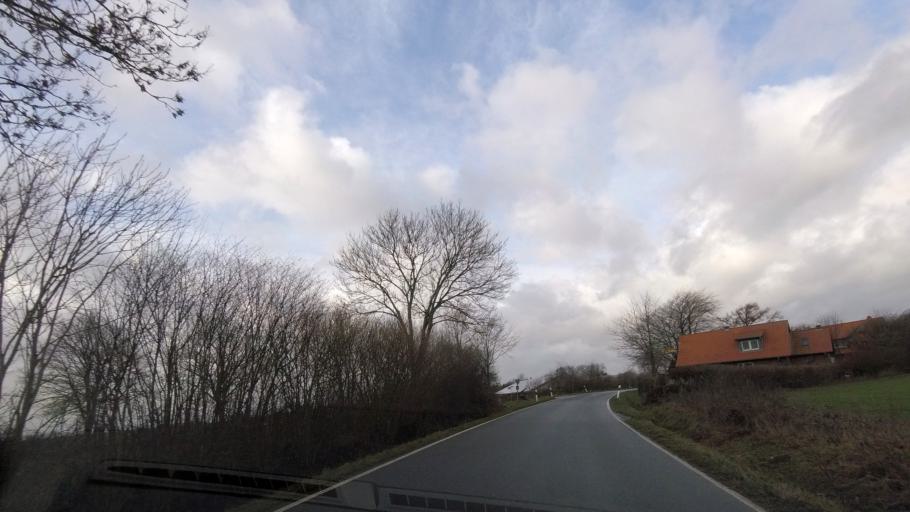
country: DE
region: Schleswig-Holstein
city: Rabenkirchen-Fauluck
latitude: 54.6332
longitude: 9.8775
